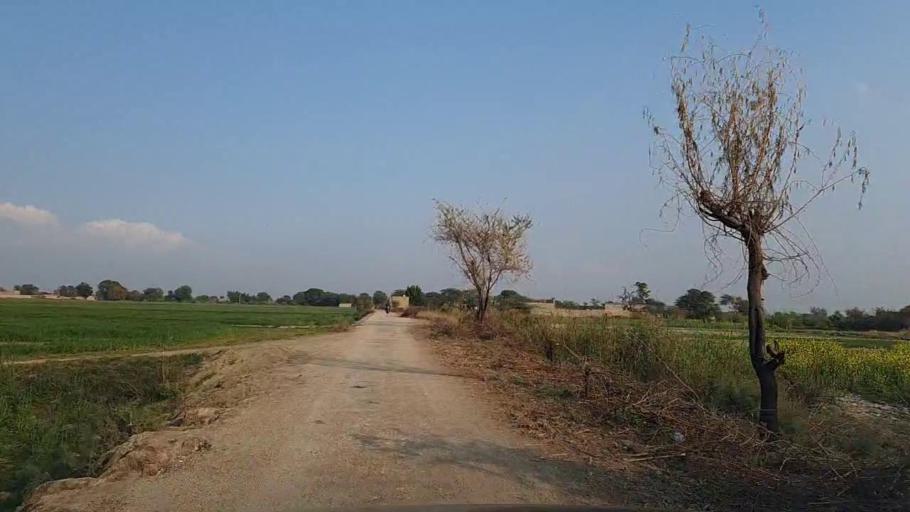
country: PK
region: Sindh
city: Jam Sahib
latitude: 26.3437
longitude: 68.5850
